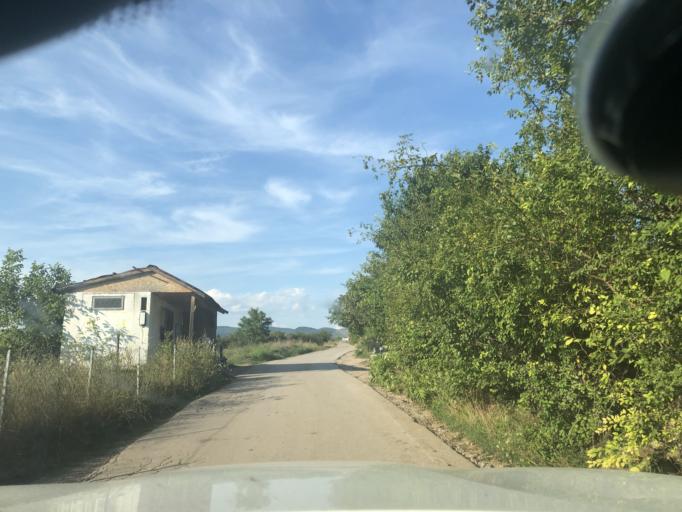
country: RS
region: Central Serbia
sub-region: Nisavski Okrug
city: Nis
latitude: 43.3232
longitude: 21.9523
